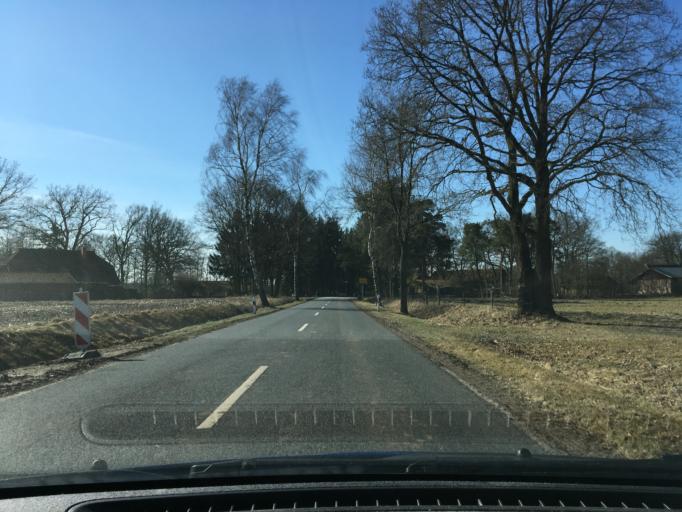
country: DE
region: Lower Saxony
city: Neuenkirchen
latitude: 53.0725
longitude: 9.7117
